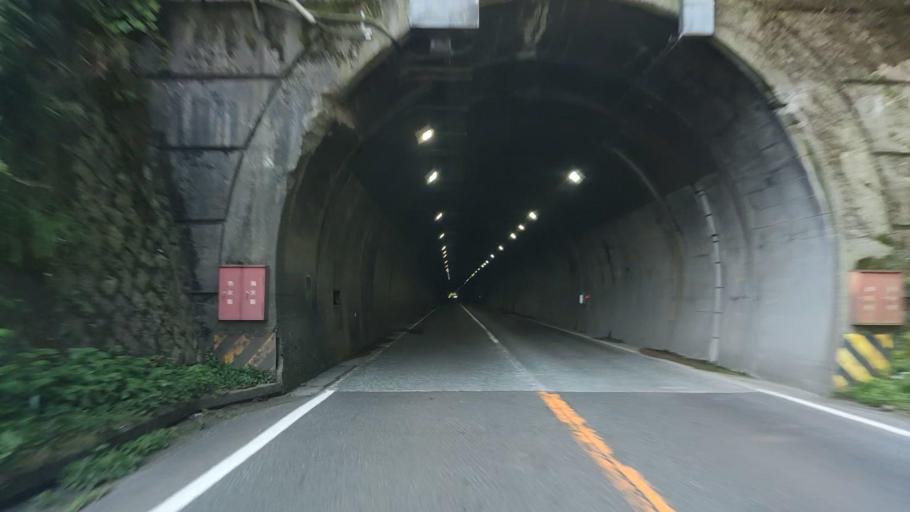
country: JP
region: Fukui
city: Tsuruga
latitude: 35.7643
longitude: 136.1048
